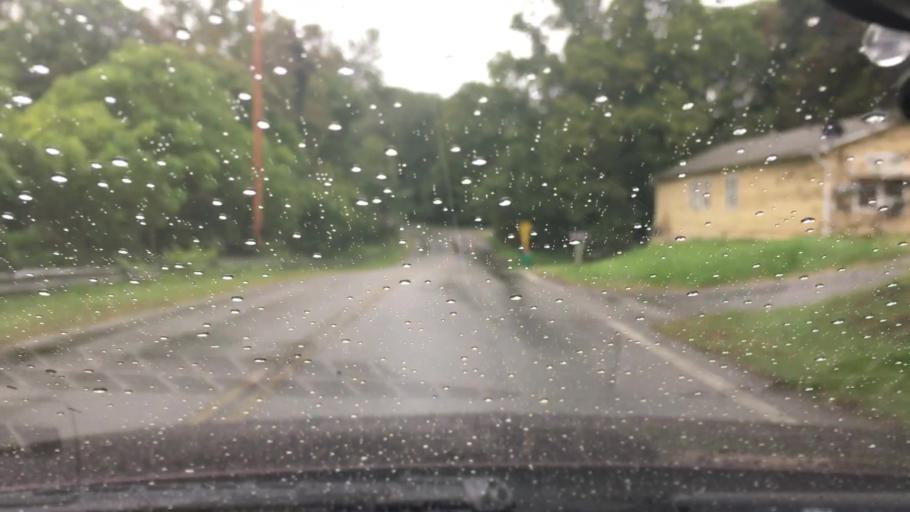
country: US
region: New York
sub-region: Dutchess County
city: Myers Corner
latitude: 41.5951
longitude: -73.8859
